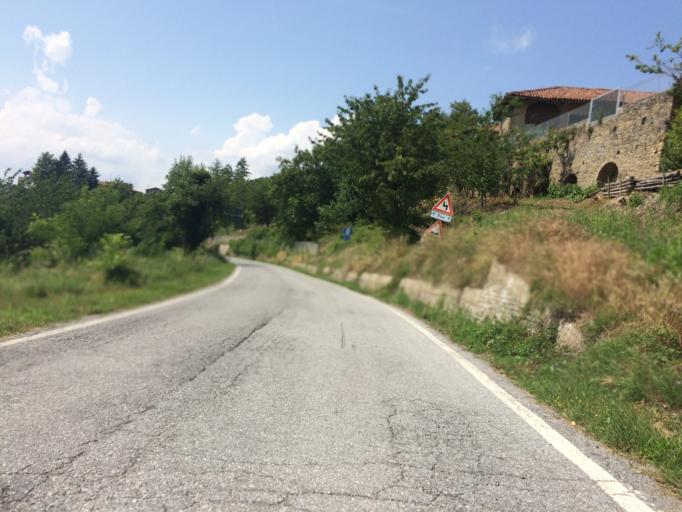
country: IT
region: Piedmont
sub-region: Provincia di Cuneo
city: Serravalle Langhe
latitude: 44.5587
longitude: 8.0588
